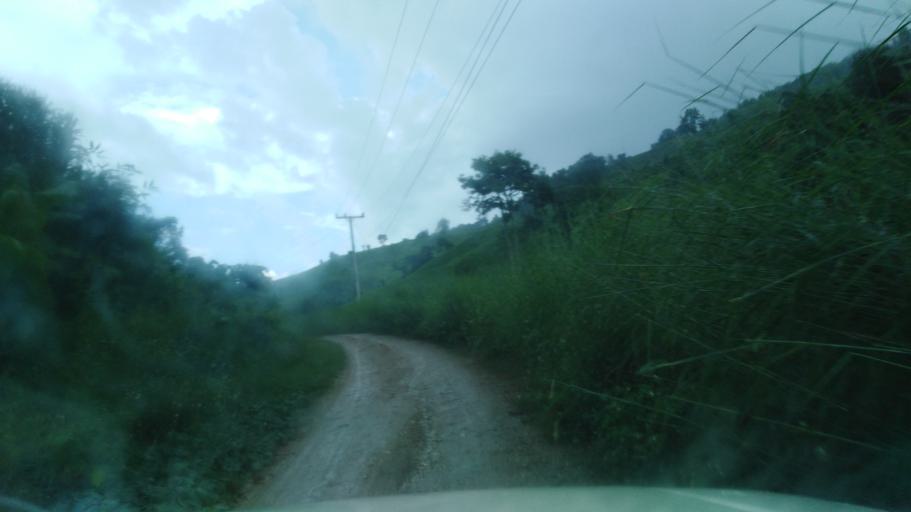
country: TH
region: Nan
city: Song Khwae
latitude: 19.7466
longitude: 100.6884
